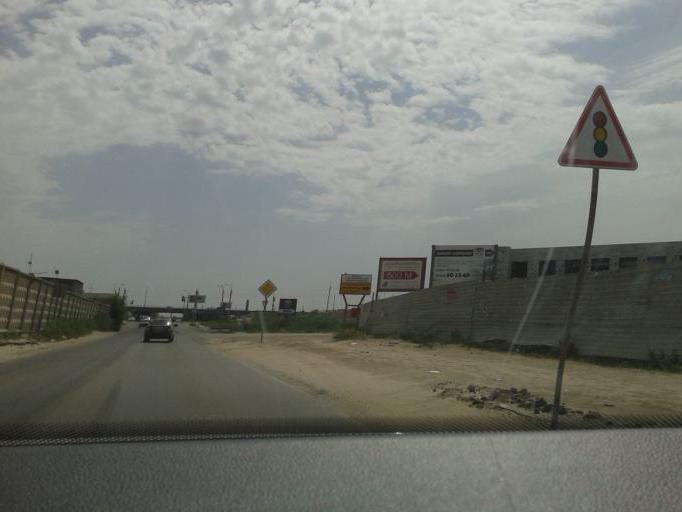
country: RU
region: Volgograd
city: Volgograd
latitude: 48.7666
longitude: 44.5119
